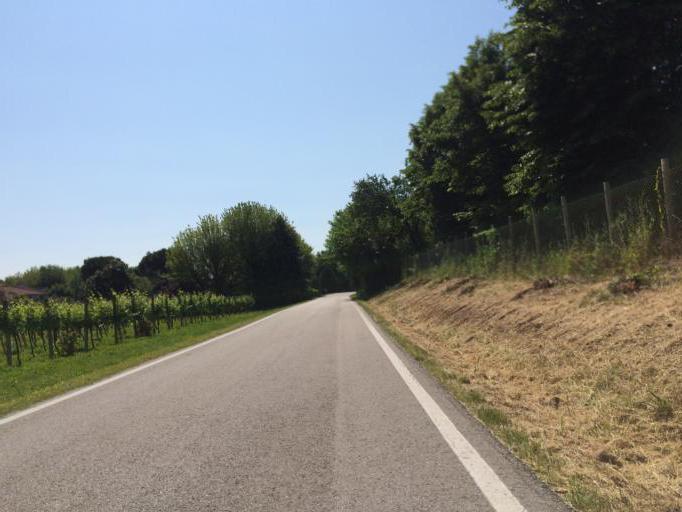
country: IT
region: Veneto
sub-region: Provincia di Vicenza
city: Montegalda
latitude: 45.4518
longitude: 11.6760
